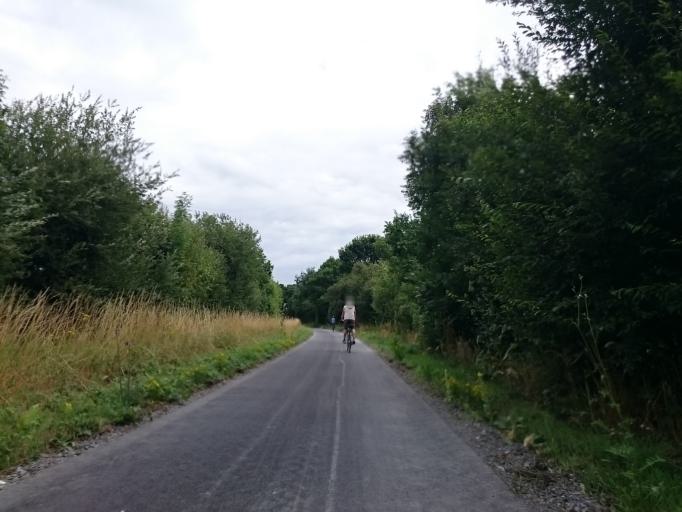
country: FR
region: Lower Normandy
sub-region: Departement du Calvados
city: Thury-Harcourt
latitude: 49.0110
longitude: -0.4720
